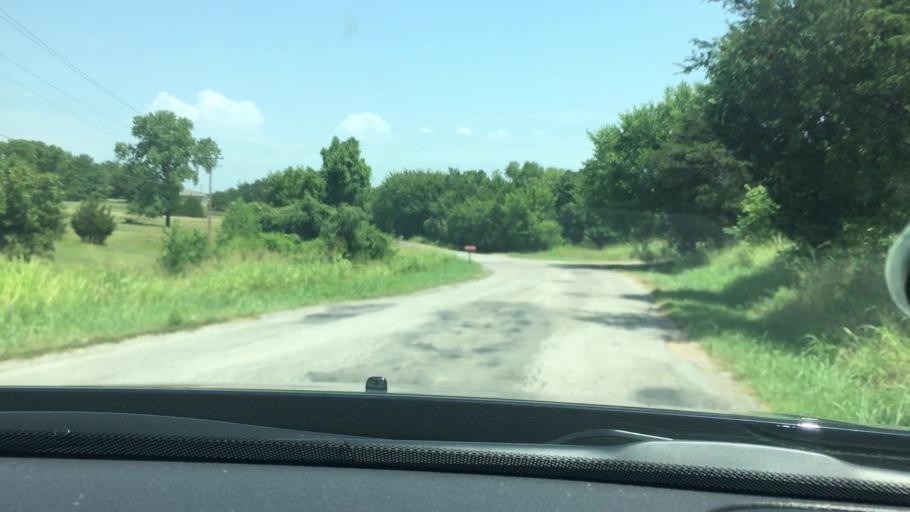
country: US
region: Oklahoma
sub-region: Pontotoc County
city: Byng
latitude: 34.8265
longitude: -96.6698
